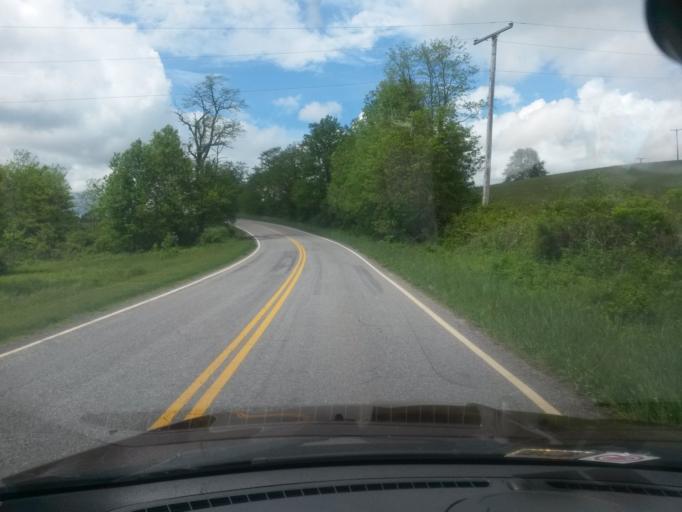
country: US
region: Virginia
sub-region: Patrick County
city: Stuart
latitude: 36.7463
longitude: -80.3902
